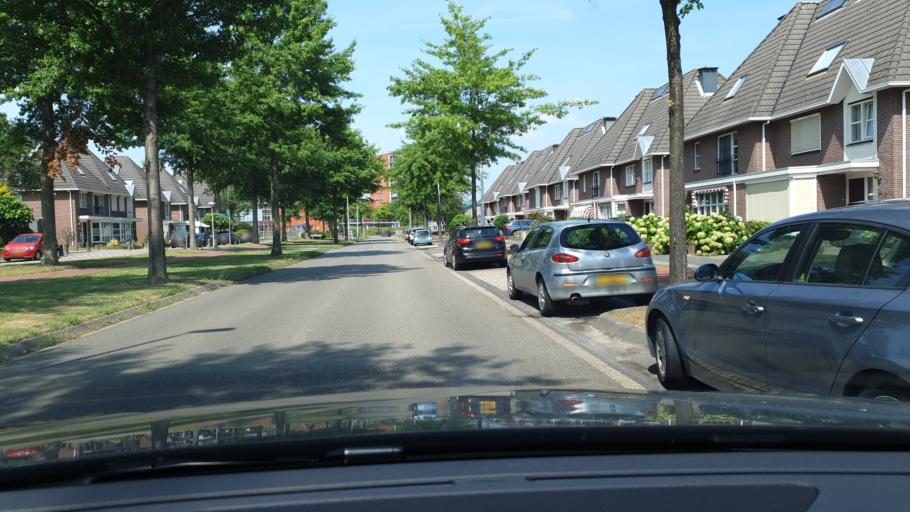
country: NL
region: North Brabant
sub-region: Gemeente Son en Breugel
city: Son
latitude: 51.4861
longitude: 5.4741
